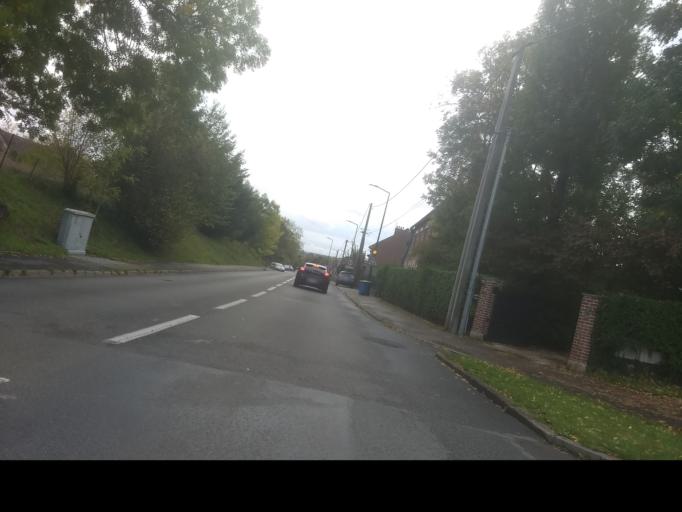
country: FR
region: Nord-Pas-de-Calais
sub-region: Departement du Pas-de-Calais
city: Sainte-Catherine
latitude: 50.3062
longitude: 2.7572
